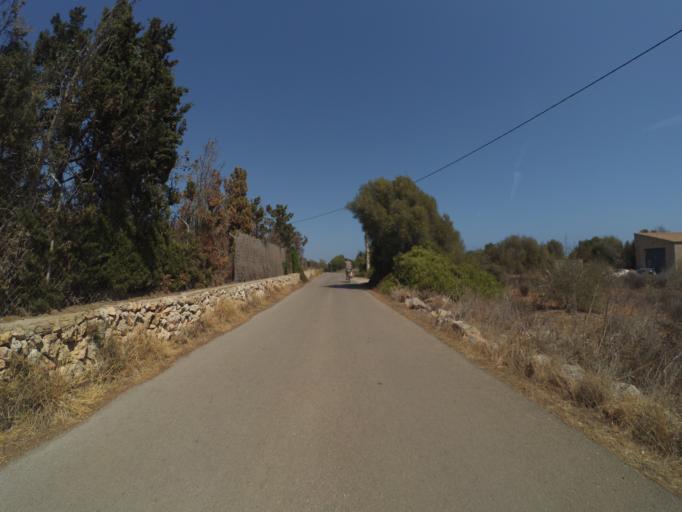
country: ES
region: Balearic Islands
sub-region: Illes Balears
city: Santanyi
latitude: 39.3912
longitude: 3.2375
